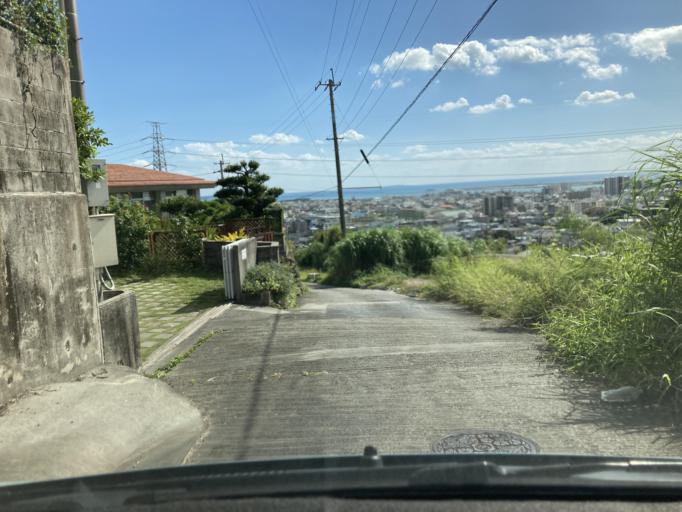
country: JP
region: Okinawa
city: Okinawa
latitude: 26.3271
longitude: 127.8178
